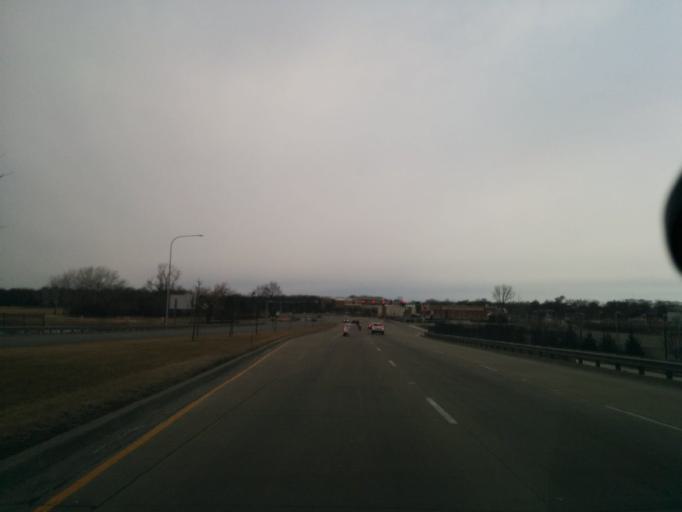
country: US
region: Illinois
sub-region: Cook County
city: Northbrook
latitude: 42.1077
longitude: -87.8704
